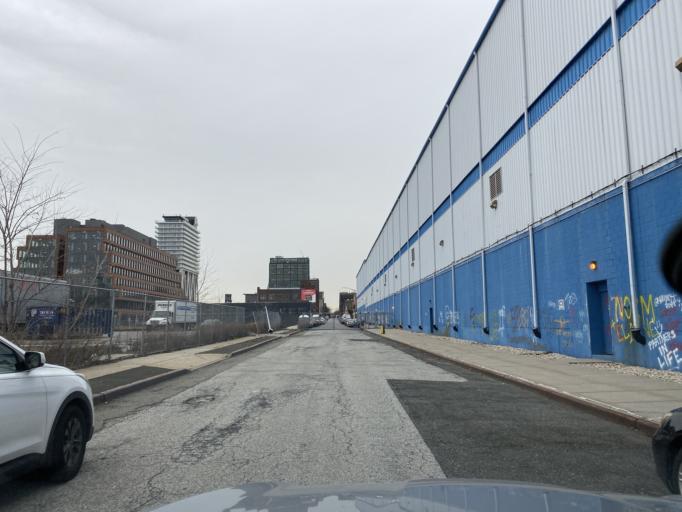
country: US
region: New York
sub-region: Queens County
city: Long Island City
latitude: 40.7238
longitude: -73.9614
